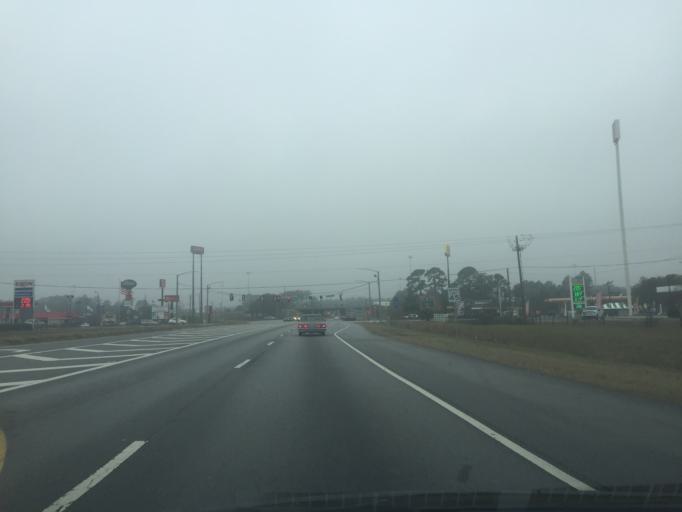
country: US
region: Georgia
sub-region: Chatham County
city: Georgetown
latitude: 32.0038
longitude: -81.2794
